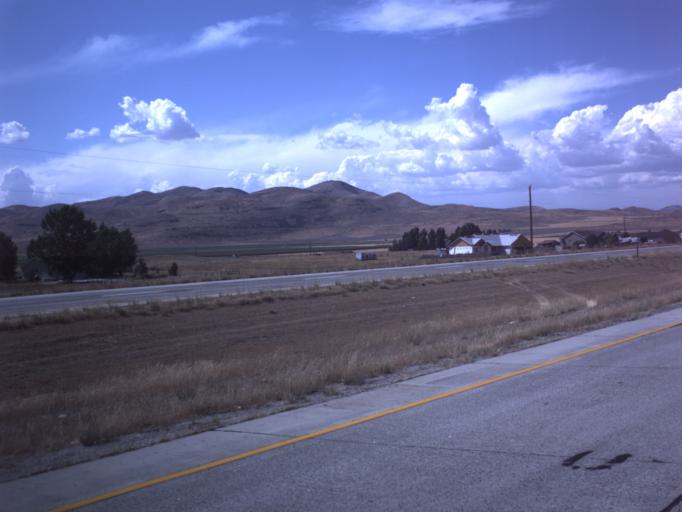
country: US
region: Utah
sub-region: Box Elder County
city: Garland
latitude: 41.7496
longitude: -112.2583
